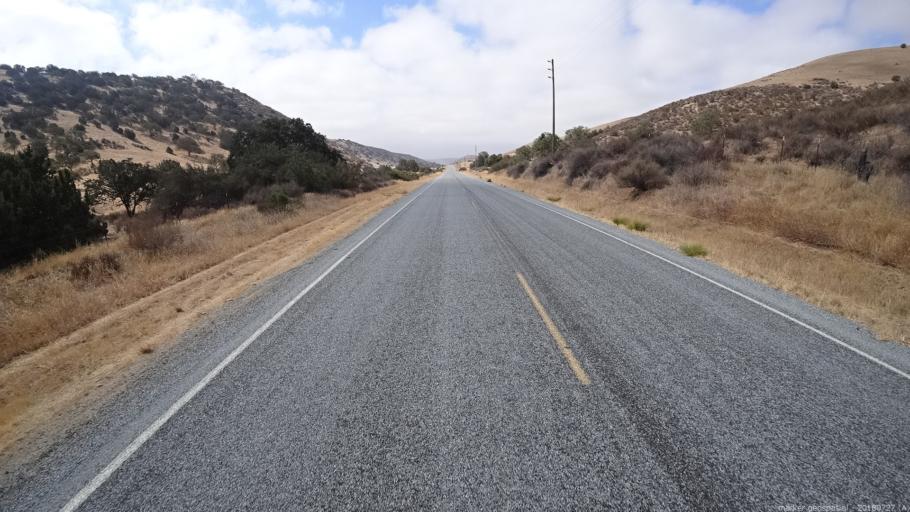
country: US
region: California
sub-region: Monterey County
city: King City
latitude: 36.2930
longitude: -121.0533
